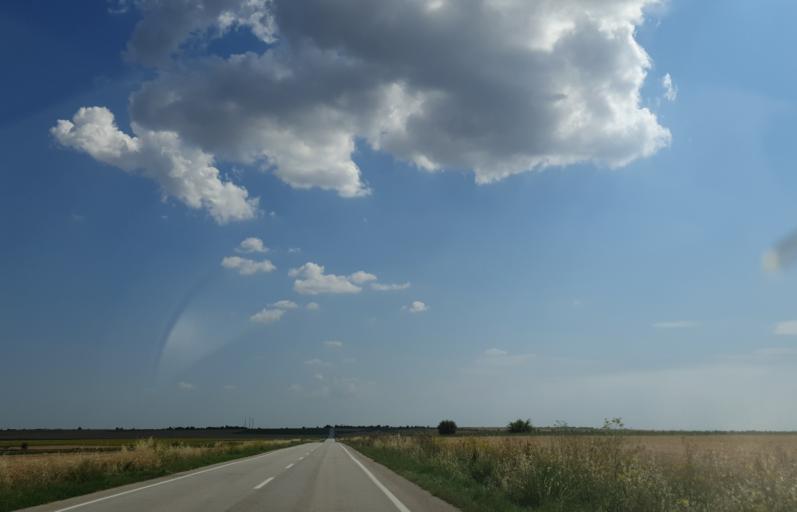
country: TR
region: Kirklareli
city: Buyukkaristiran
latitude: 41.3967
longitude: 27.5734
